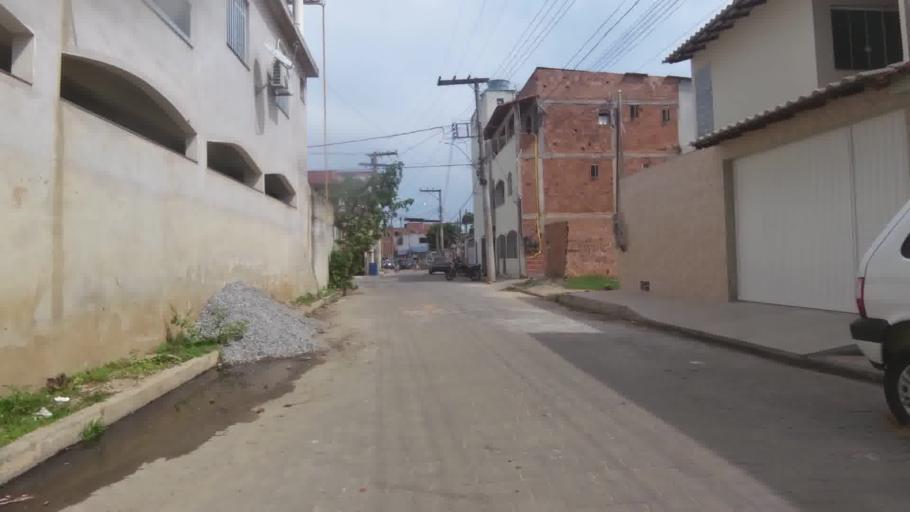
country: BR
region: Espirito Santo
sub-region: Piuma
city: Piuma
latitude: -20.8405
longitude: -40.7432
